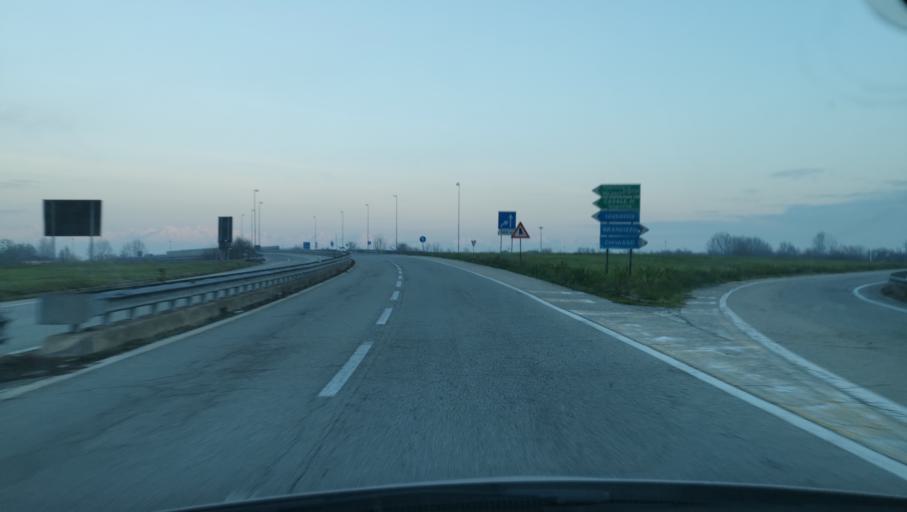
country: IT
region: Piedmont
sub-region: Provincia di Torino
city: Brandizzo
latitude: 45.1849
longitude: 7.8596
